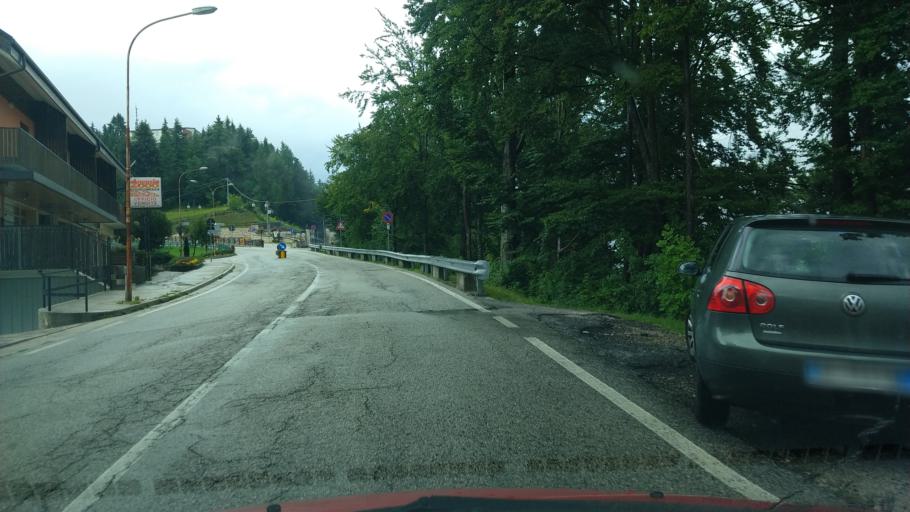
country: IT
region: Veneto
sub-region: Provincia di Vicenza
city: Tonezza del Cimone
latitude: 45.8601
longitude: 11.3476
